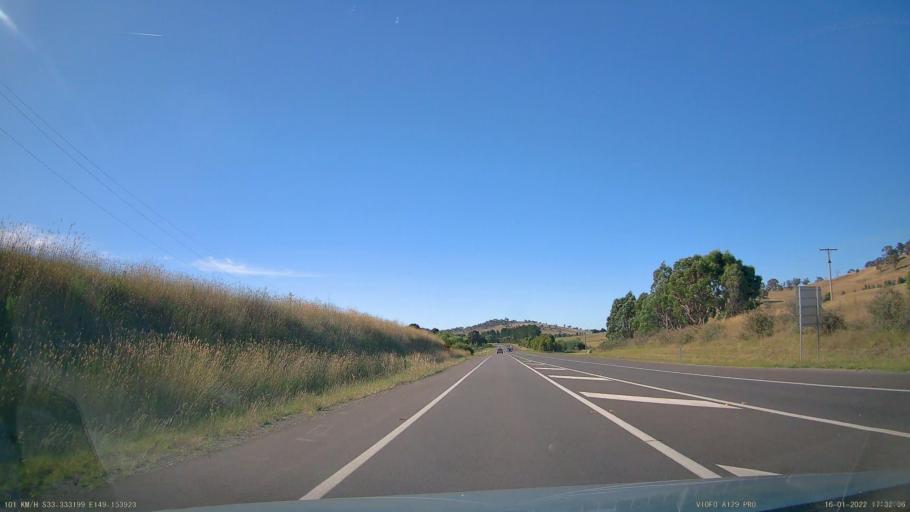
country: AU
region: New South Wales
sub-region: Orange Municipality
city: Orange
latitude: -33.3330
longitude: 149.1538
